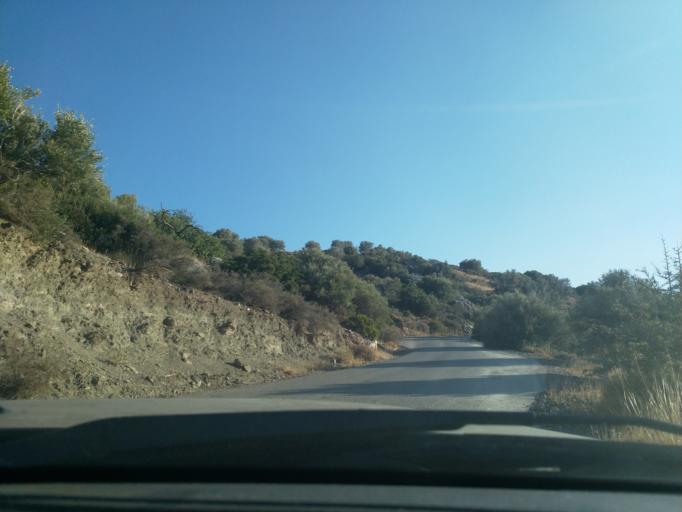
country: GR
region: Crete
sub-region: Nomos Rethymnis
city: Agia Galini
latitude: 35.1138
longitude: 24.5662
